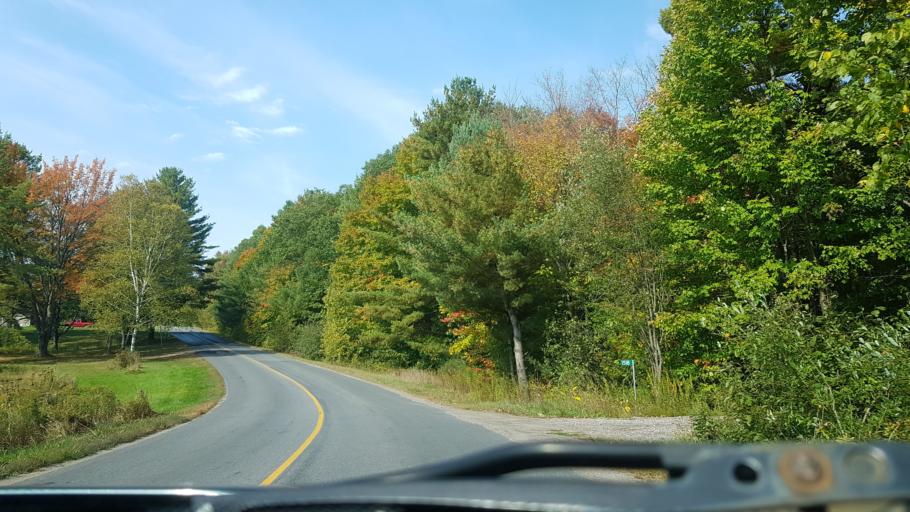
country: CA
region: Ontario
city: Gravenhurst
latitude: 44.7870
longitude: -79.2346
